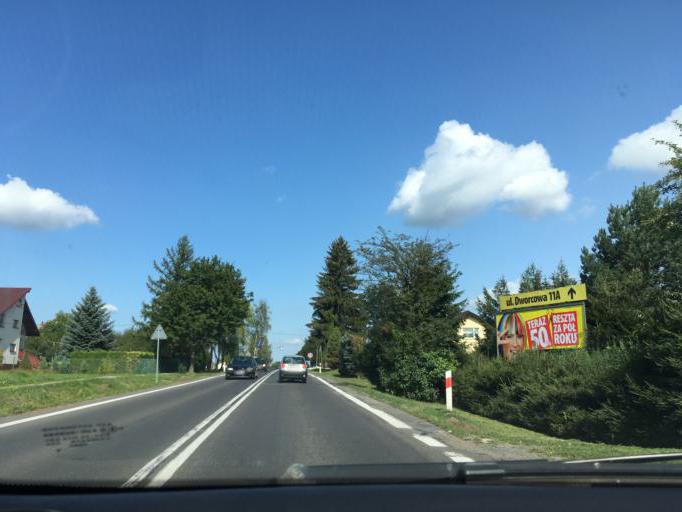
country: PL
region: Subcarpathian Voivodeship
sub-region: Powiat sanocki
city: Sanok
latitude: 49.5313
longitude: 22.2306
